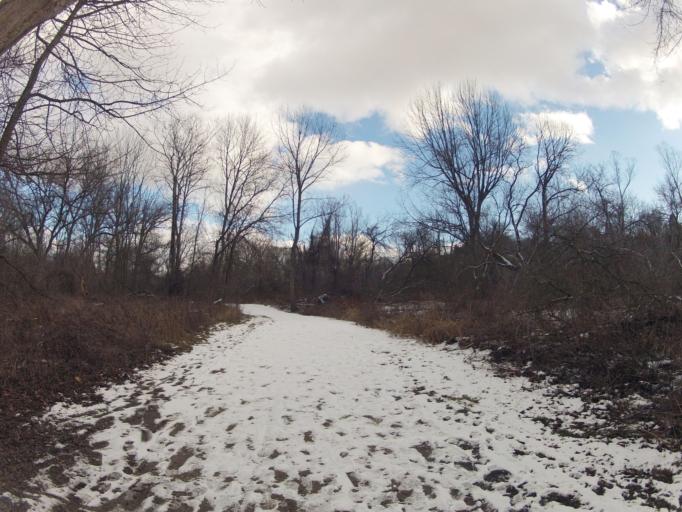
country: CA
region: Ontario
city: Mississauga
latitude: 43.5634
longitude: -79.6786
